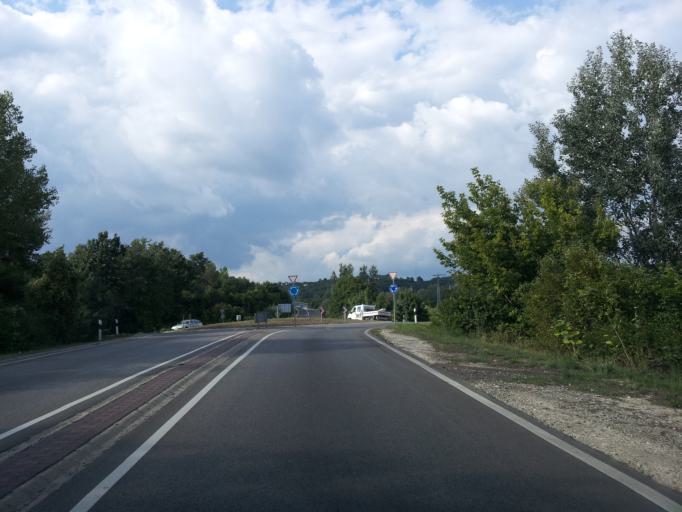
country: HU
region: Pest
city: Dunabogdany
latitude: 47.8142
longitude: 19.0929
